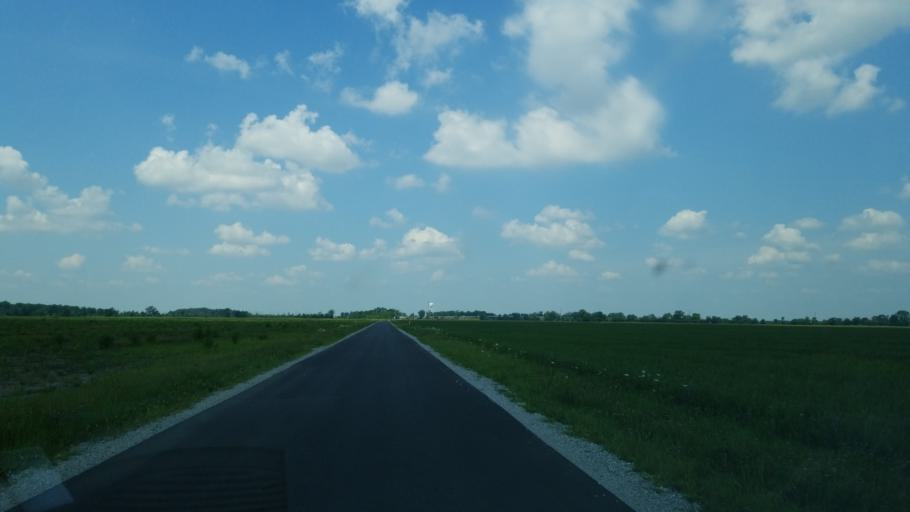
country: US
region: Ohio
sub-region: Wood County
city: North Baltimore
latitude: 41.2681
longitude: -83.6255
